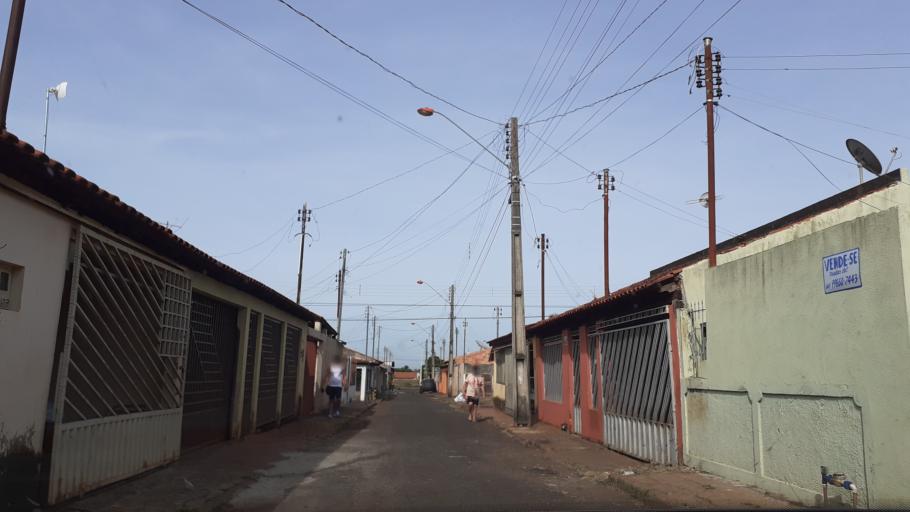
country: BR
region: Goias
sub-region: Itumbiara
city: Itumbiara
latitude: -18.4151
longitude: -49.2397
